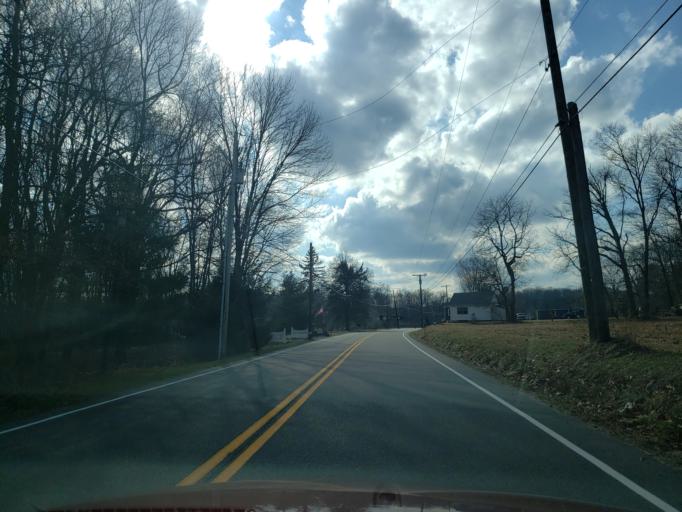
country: US
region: New Jersey
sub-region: Hunterdon County
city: Flemington
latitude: 40.4643
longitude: -74.9244
